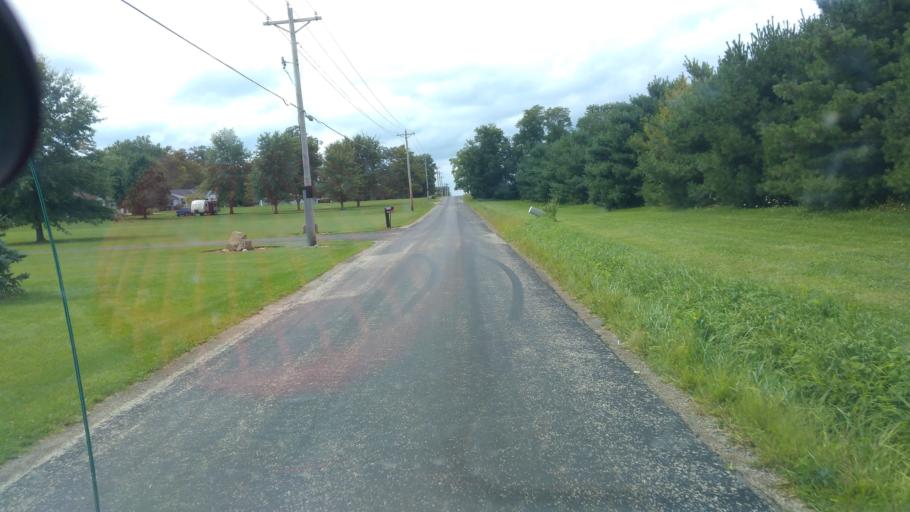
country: US
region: Ohio
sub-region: Ashland County
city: Ashland
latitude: 40.8218
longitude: -82.3547
